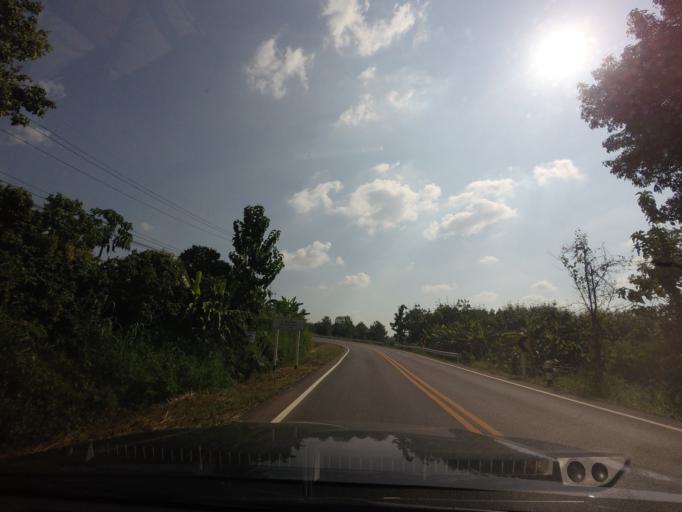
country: TH
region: Nan
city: Santi Suk
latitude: 18.9672
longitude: 100.9237
